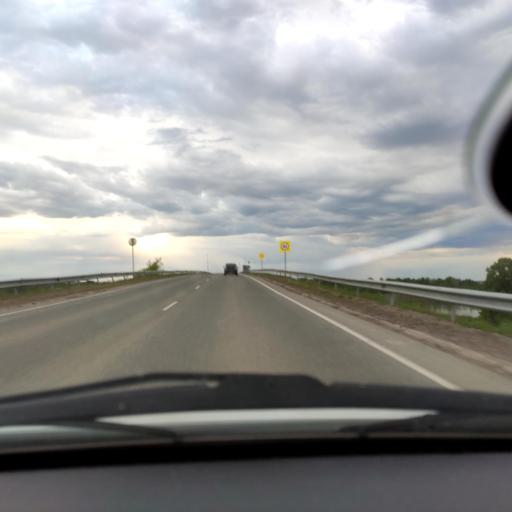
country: RU
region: Bashkortostan
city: Dyurtyuli
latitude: 55.5340
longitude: 54.8540
